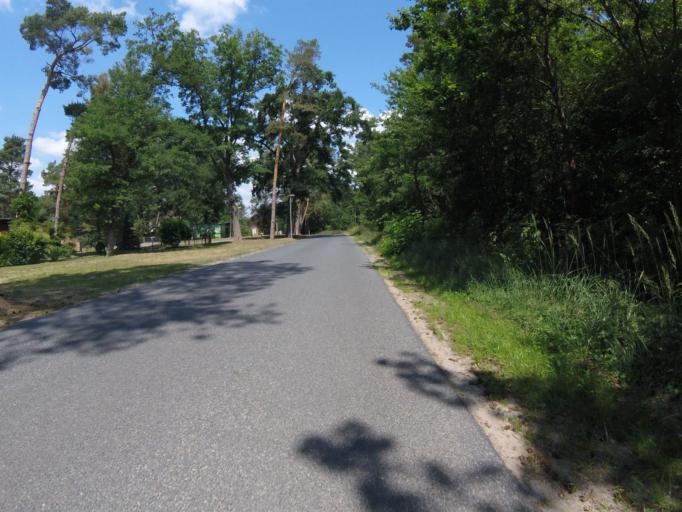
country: DE
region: Brandenburg
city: Bestensee
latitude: 52.2807
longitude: 13.6574
